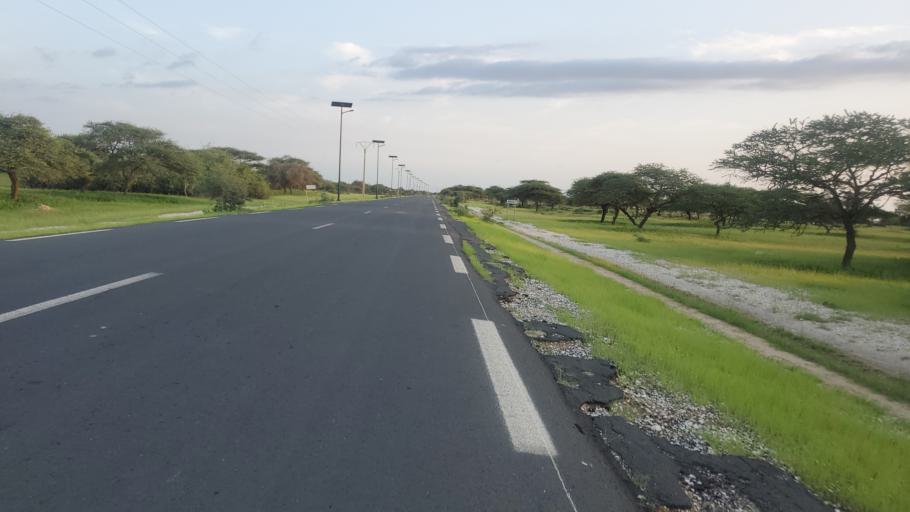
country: SN
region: Saint-Louis
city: Saint-Louis
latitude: 16.1493
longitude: -16.4097
